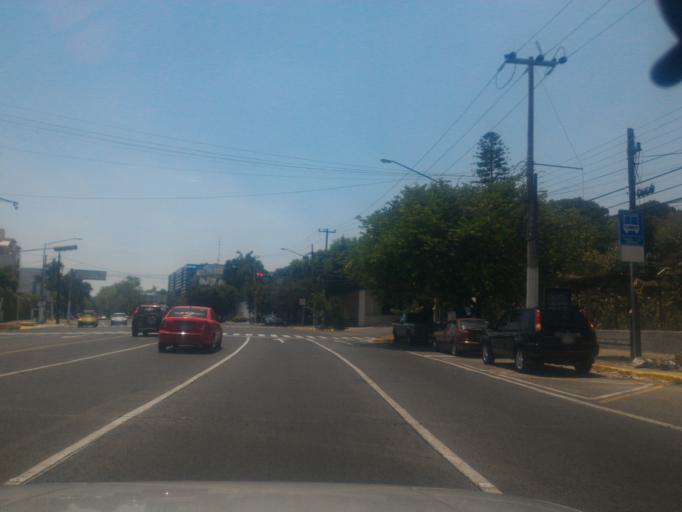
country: MX
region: Jalisco
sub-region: Zapopan
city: Zapopan
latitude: 20.7140
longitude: -103.3848
